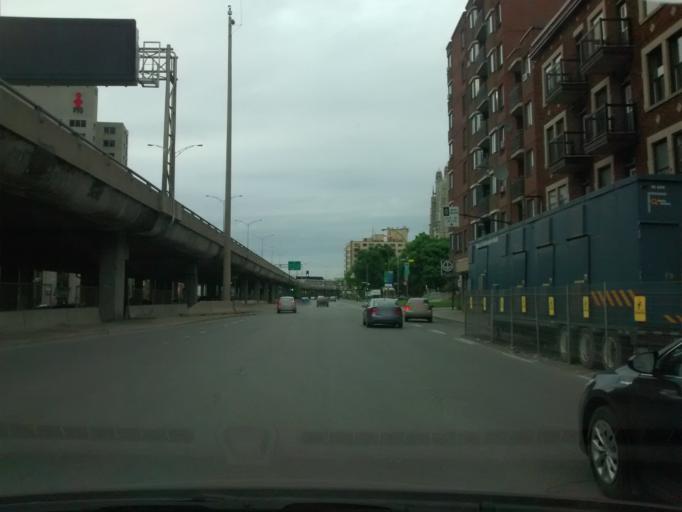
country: CA
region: Quebec
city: Mont-Royal
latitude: 45.5451
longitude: -73.6389
